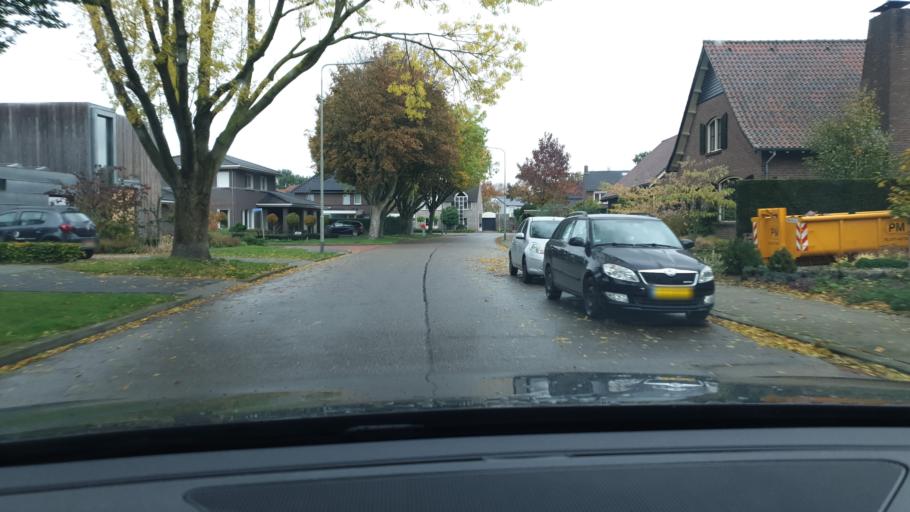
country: NL
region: Limburg
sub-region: Gemeente Peel en Maas
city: Maasbree
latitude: 51.4103
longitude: 6.0310
